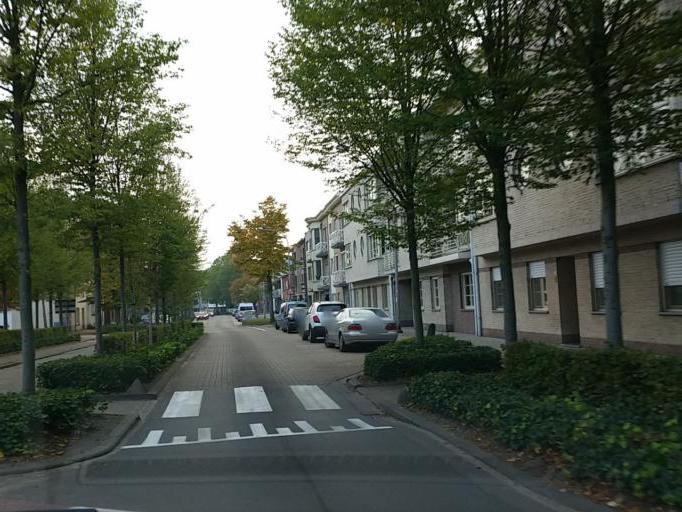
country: BE
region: Flanders
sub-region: Provincie Antwerpen
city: Brasschaat
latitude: 51.3039
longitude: 4.4855
